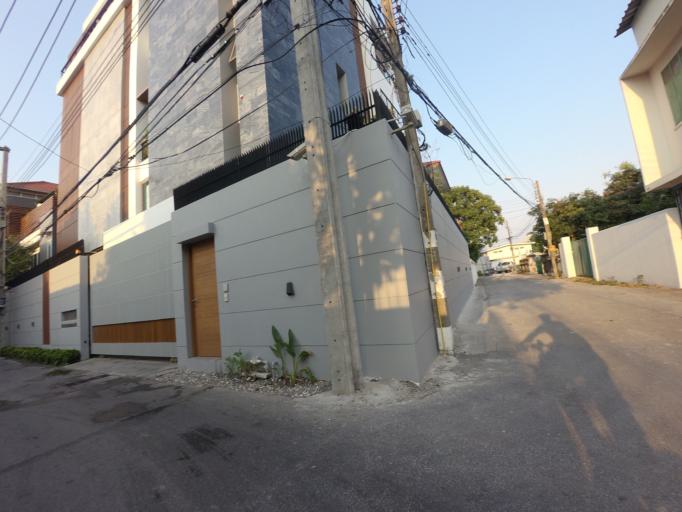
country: TH
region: Bangkok
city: Watthana
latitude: 13.7224
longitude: 100.5893
